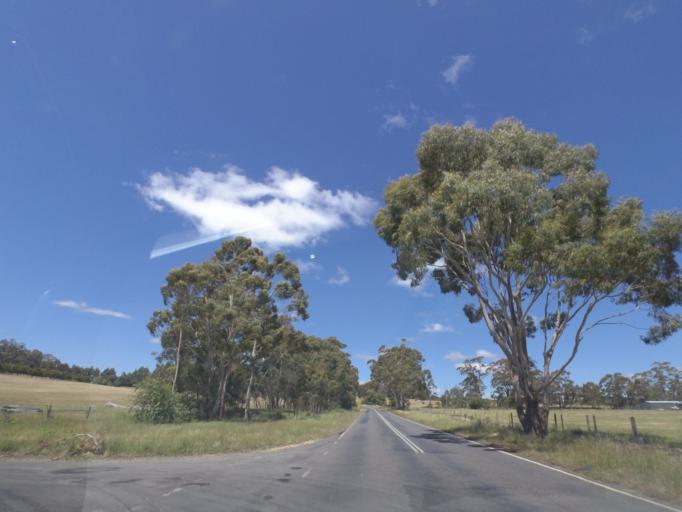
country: AU
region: Victoria
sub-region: Mount Alexander
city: Castlemaine
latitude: -37.2914
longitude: 144.2533
